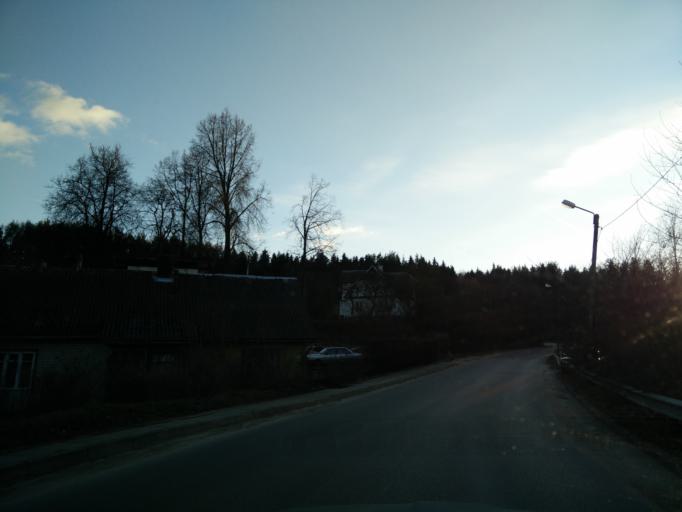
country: LT
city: Skaidiskes
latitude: 54.6914
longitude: 25.3974
